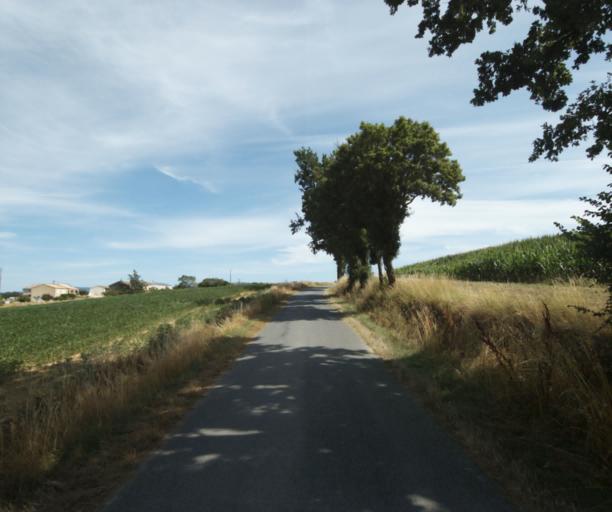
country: FR
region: Midi-Pyrenees
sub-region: Departement du Tarn
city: Soreze
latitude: 43.5116
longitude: 2.0430
